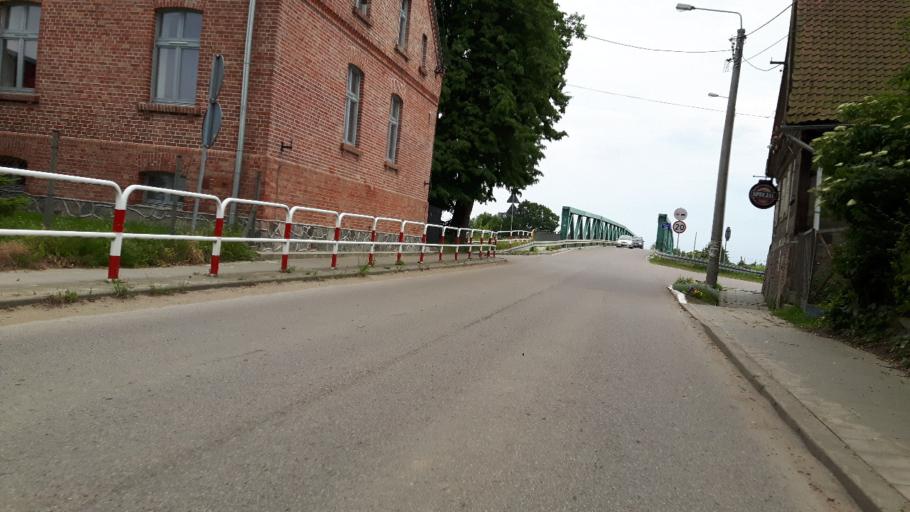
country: PL
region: Warmian-Masurian Voivodeship
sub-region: Powiat elblaski
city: Elblag
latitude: 54.1902
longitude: 19.3134
